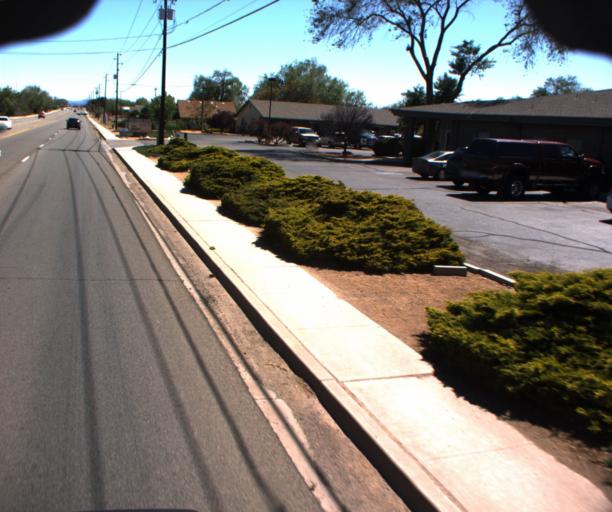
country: US
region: Arizona
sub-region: Yavapai County
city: Chino Valley
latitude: 34.7527
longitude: -112.4542
